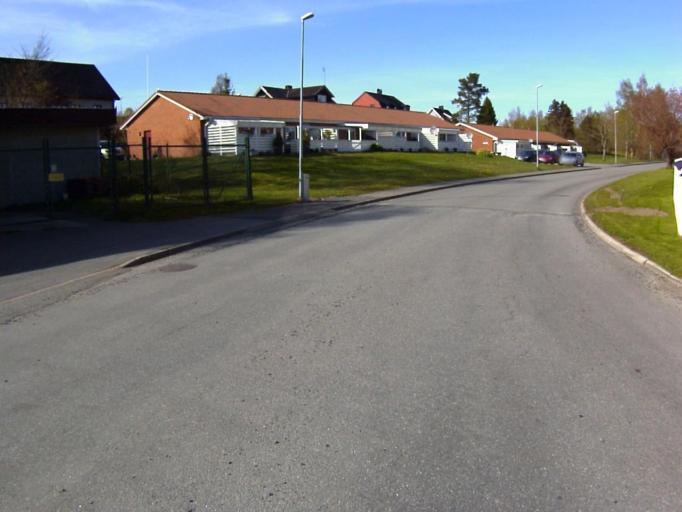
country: SE
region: Skane
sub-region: Kristianstads Kommun
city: Onnestad
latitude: 55.9935
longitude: 14.0361
